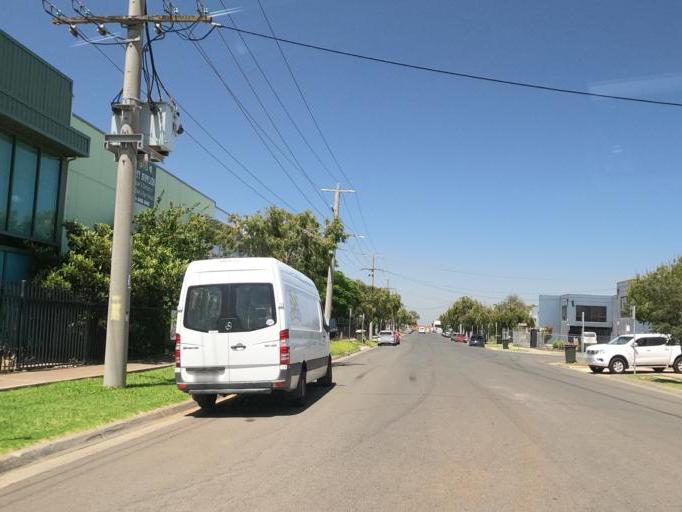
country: AU
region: Victoria
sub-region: Whittlesea
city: Lalor
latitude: -37.6472
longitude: 145.0122
